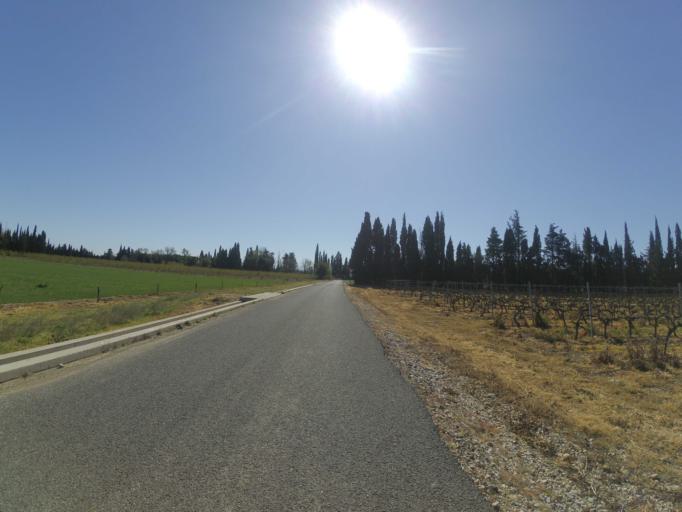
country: FR
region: Languedoc-Roussillon
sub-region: Departement des Pyrenees-Orientales
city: Corneilla-la-Riviere
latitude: 42.6771
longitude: 2.7258
